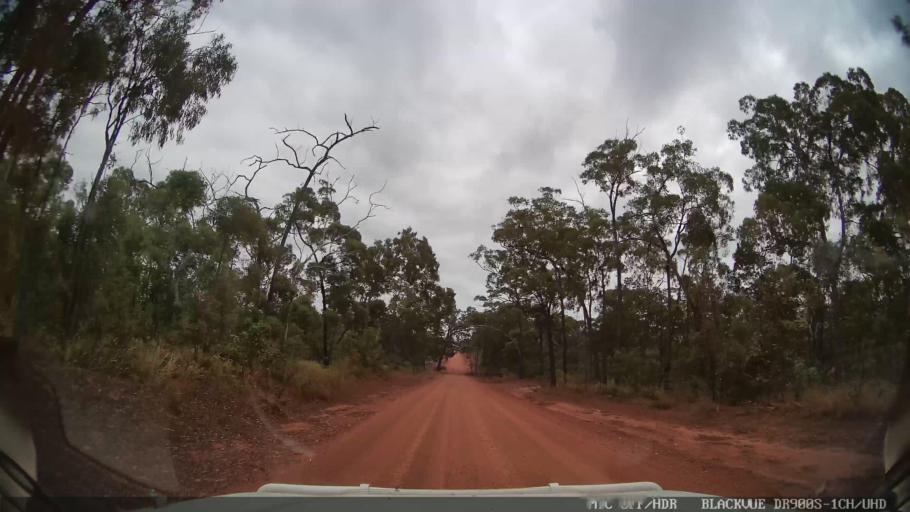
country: AU
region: Queensland
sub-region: Cook
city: Cooktown
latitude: -15.2649
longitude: 144.9517
